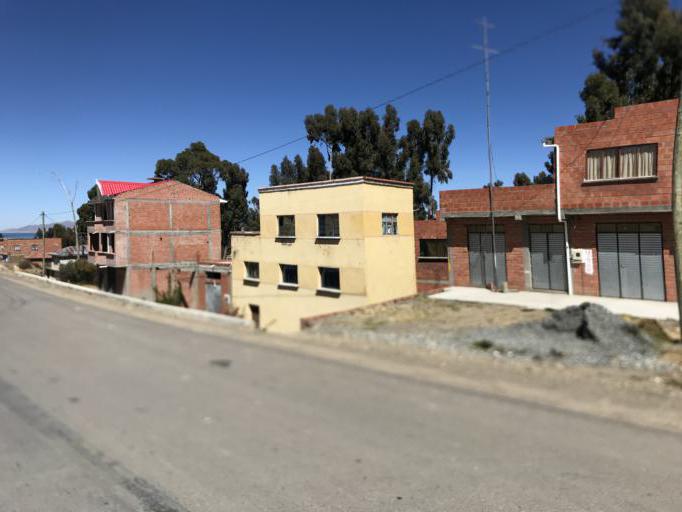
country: BO
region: La Paz
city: Huatajata
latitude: -16.1988
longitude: -68.7146
